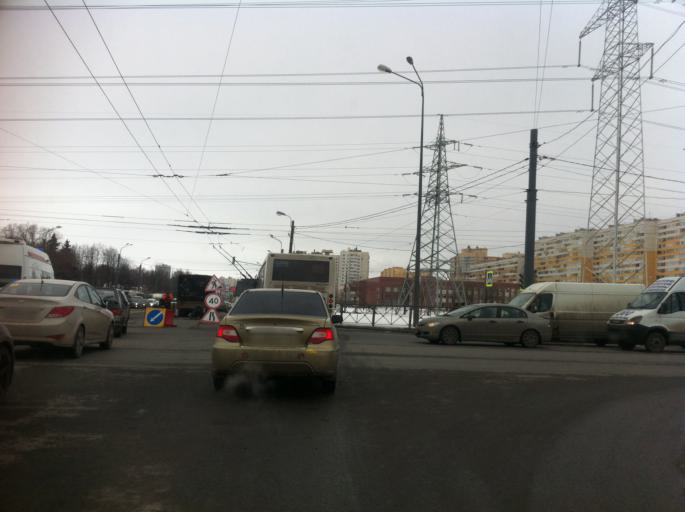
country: RU
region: St.-Petersburg
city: Uritsk
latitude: 59.8461
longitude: 30.1756
